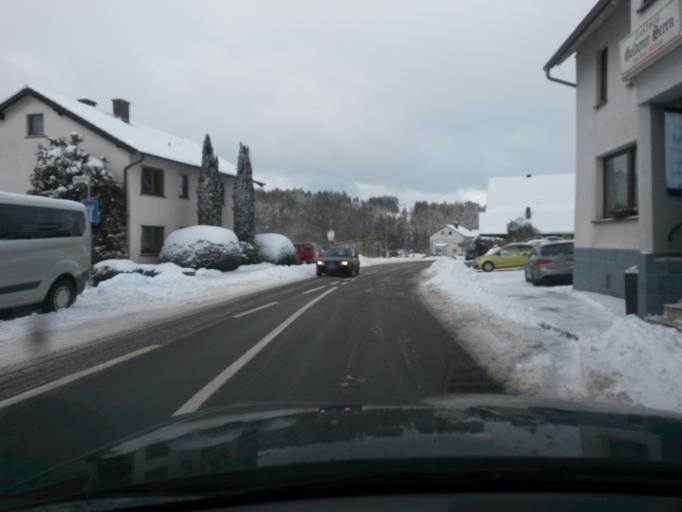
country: DE
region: Thuringia
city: Birx
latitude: 50.5270
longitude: 10.0140
